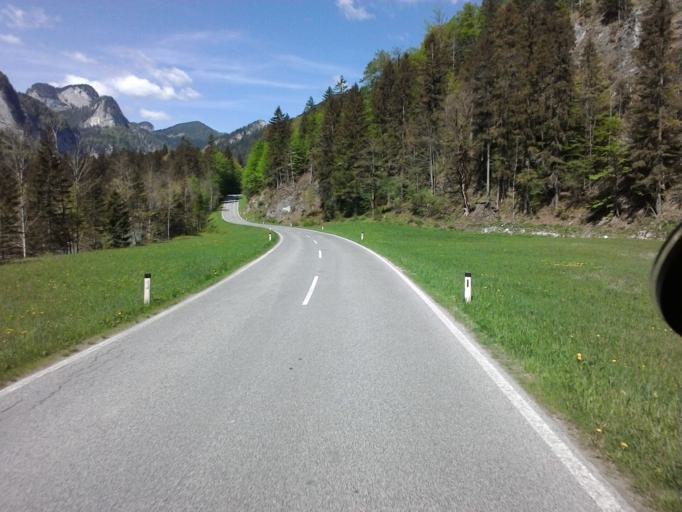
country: AT
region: Styria
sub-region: Politischer Bezirk Liezen
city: Wildalpen
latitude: 47.6716
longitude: 14.9748
